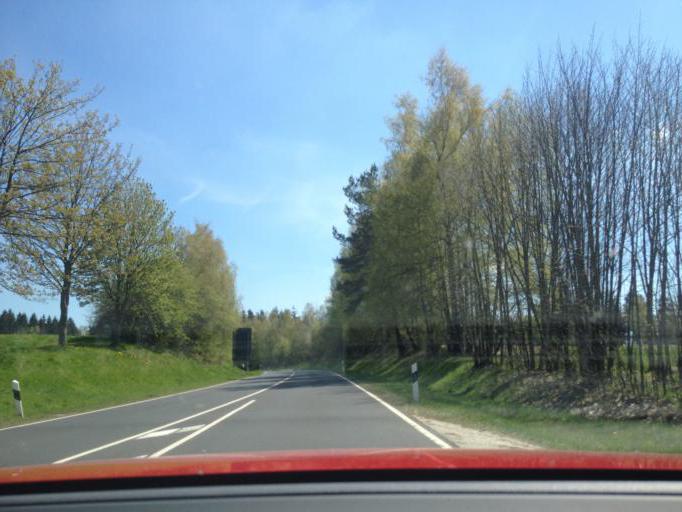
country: DE
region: Bavaria
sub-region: Upper Franconia
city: Kirchenlamitz
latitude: 50.1468
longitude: 11.9604
